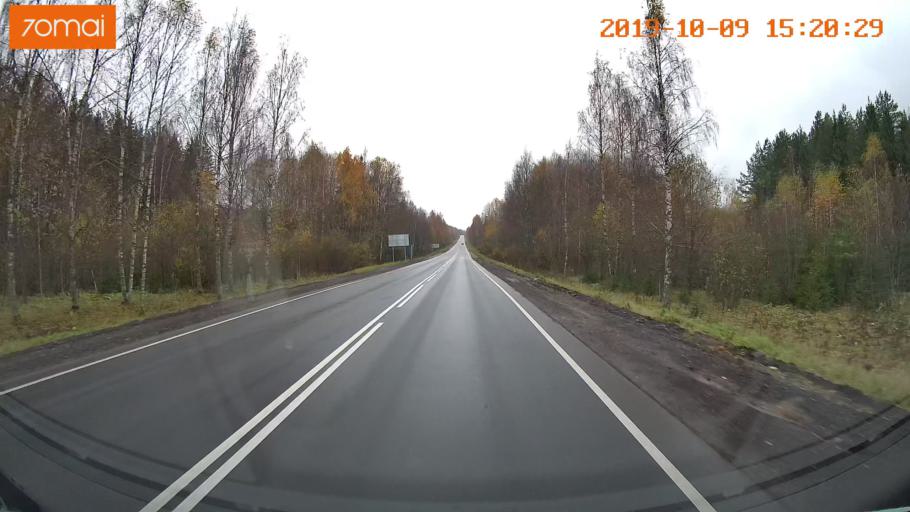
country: RU
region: Kostroma
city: Susanino
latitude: 58.0639
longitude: 41.5370
